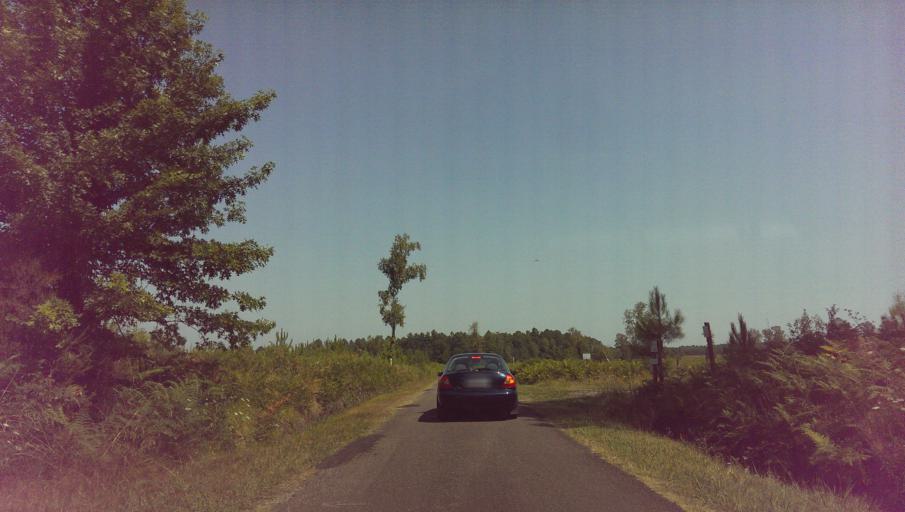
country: FR
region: Aquitaine
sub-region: Departement des Landes
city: Sarbazan
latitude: 44.0190
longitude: -0.1958
